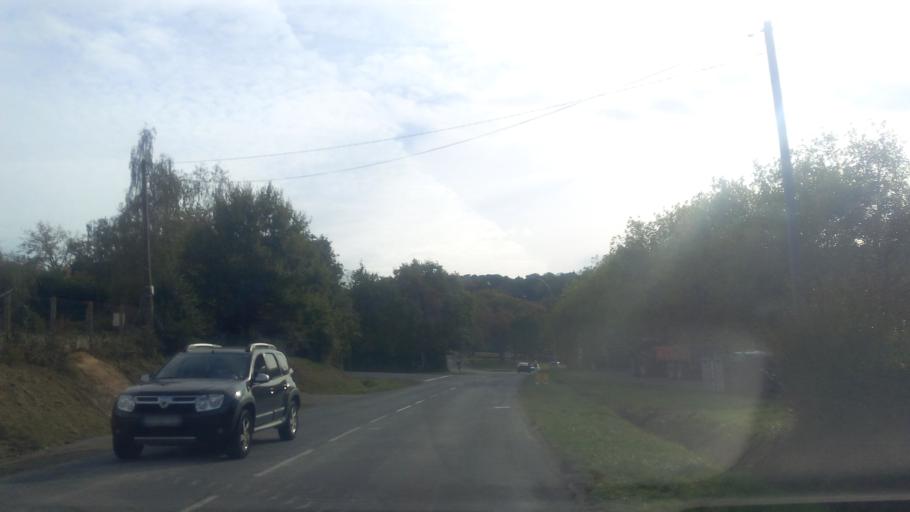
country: FR
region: Brittany
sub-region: Departement du Morbihan
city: Saint-Perreux
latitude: 47.6726
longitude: -2.0880
